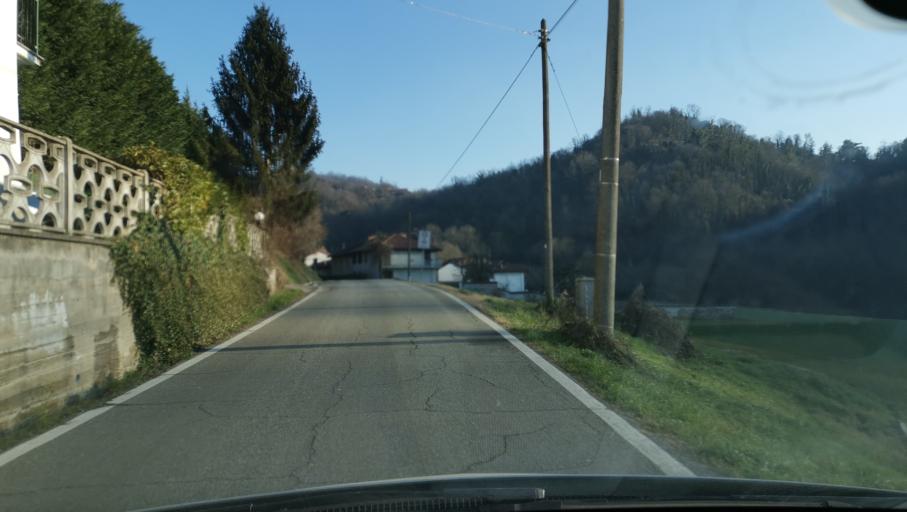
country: IT
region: Piedmont
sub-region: Provincia di Torino
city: San Raffaele Cimena
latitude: 45.1347
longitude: 7.8480
